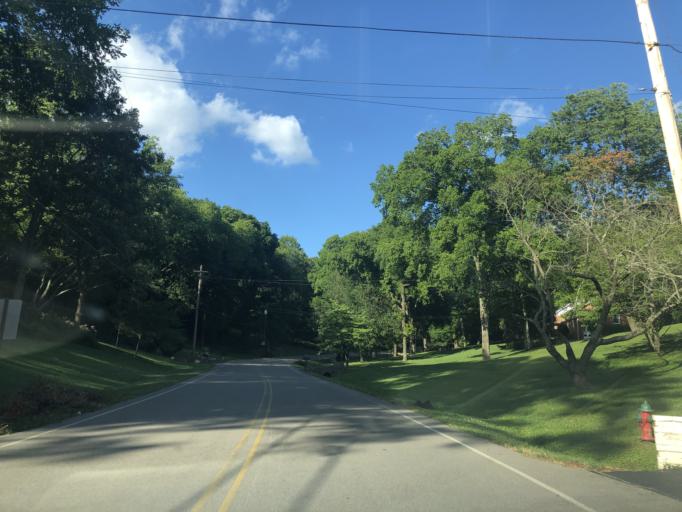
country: US
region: Tennessee
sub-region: Davidson County
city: Forest Hills
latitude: 36.0728
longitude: -86.8213
